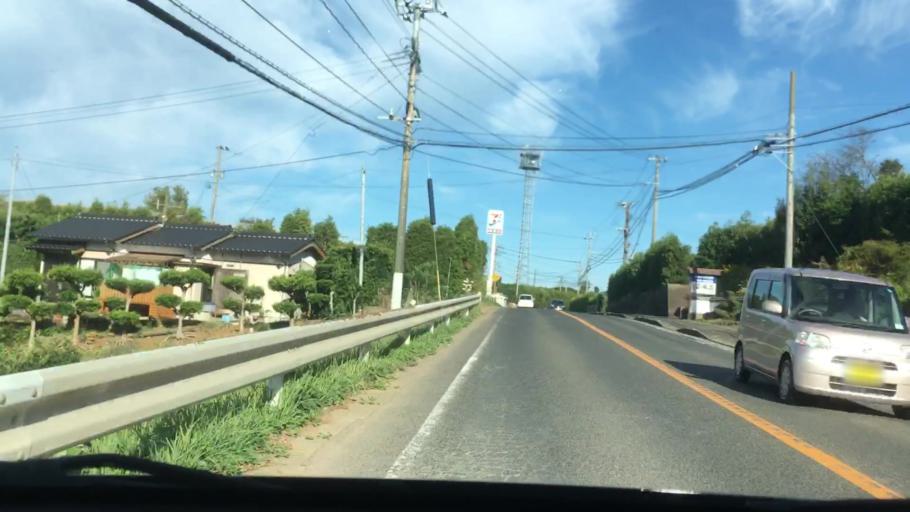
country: JP
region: Nagasaki
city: Sasebo
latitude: 33.0705
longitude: 129.7620
